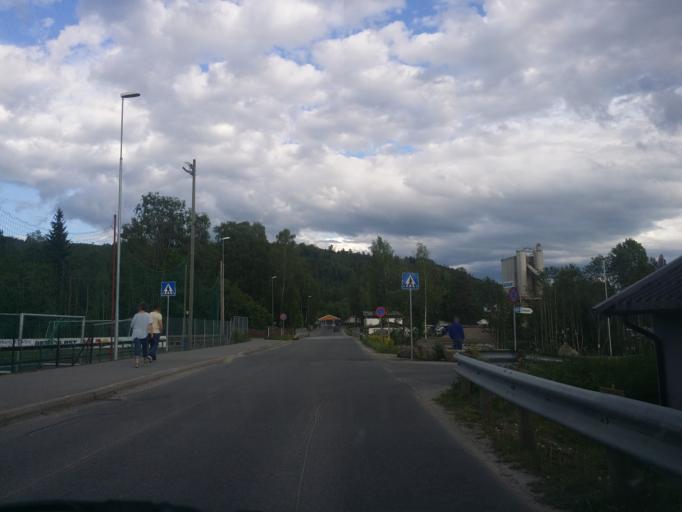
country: NO
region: Hedmark
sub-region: Ringsaker
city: Brumunddal
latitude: 60.8910
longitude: 10.9473
